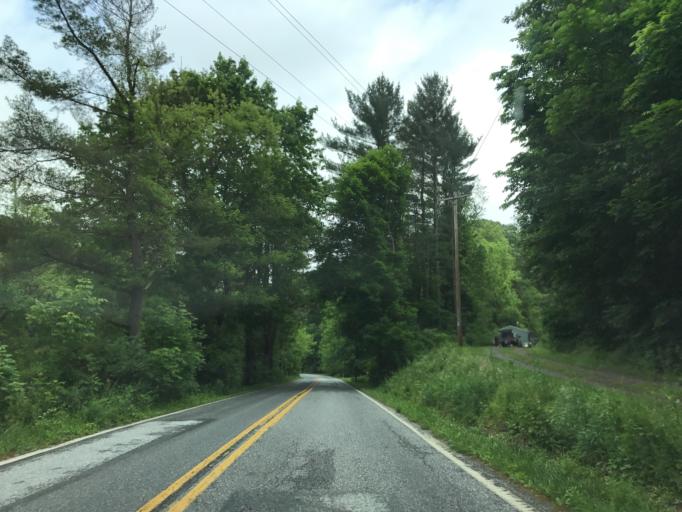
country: US
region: Pennsylvania
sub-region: York County
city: Loganville
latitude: 39.8392
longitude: -76.6656
